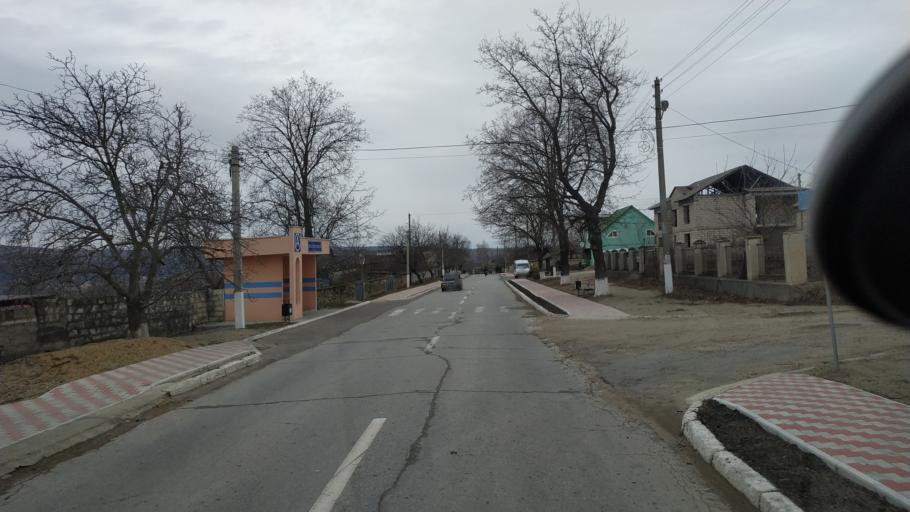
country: MD
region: Telenesti
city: Cocieri
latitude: 47.3396
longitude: 29.0968
